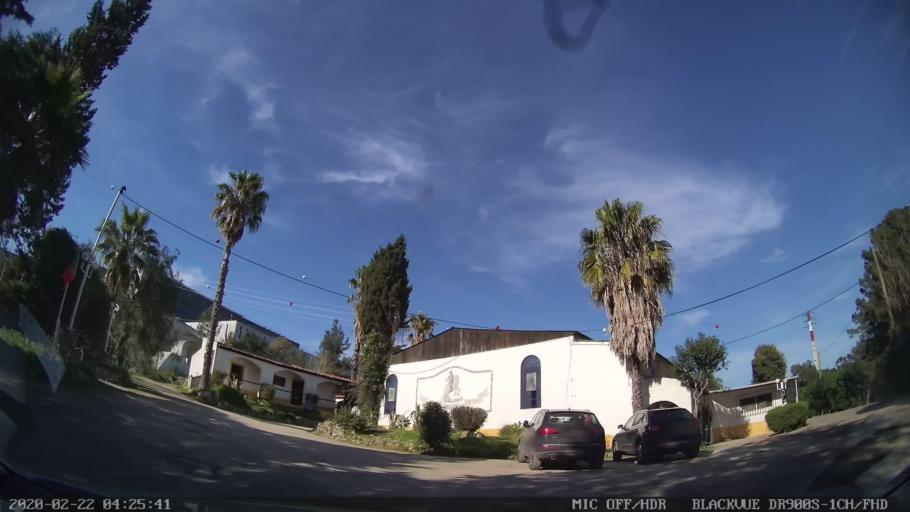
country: PT
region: Lisbon
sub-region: Vila Franca de Xira
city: Castanheira do Ribatejo
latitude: 38.9761
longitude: -8.9832
